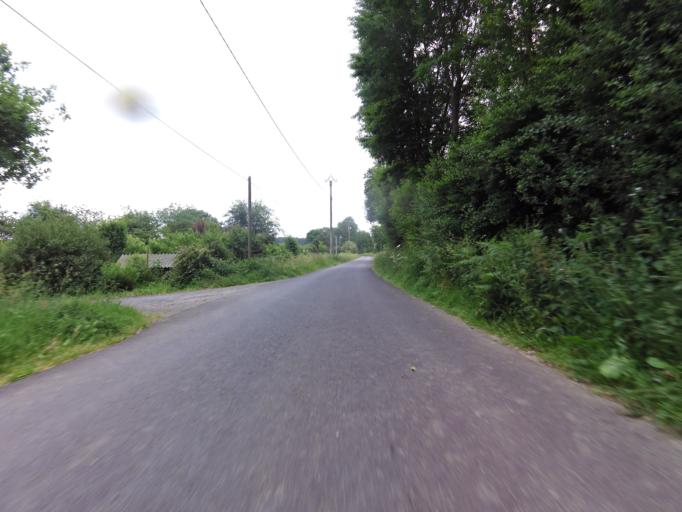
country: FR
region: Brittany
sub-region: Departement du Morbihan
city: Pluherlin
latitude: 47.7185
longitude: -2.3835
